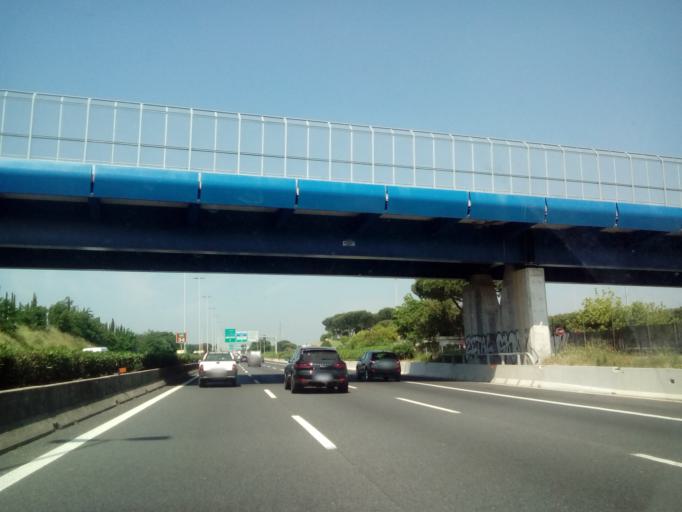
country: IT
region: Latium
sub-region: Citta metropolitana di Roma Capitale
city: Selcetta
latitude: 41.7964
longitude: 12.4907
